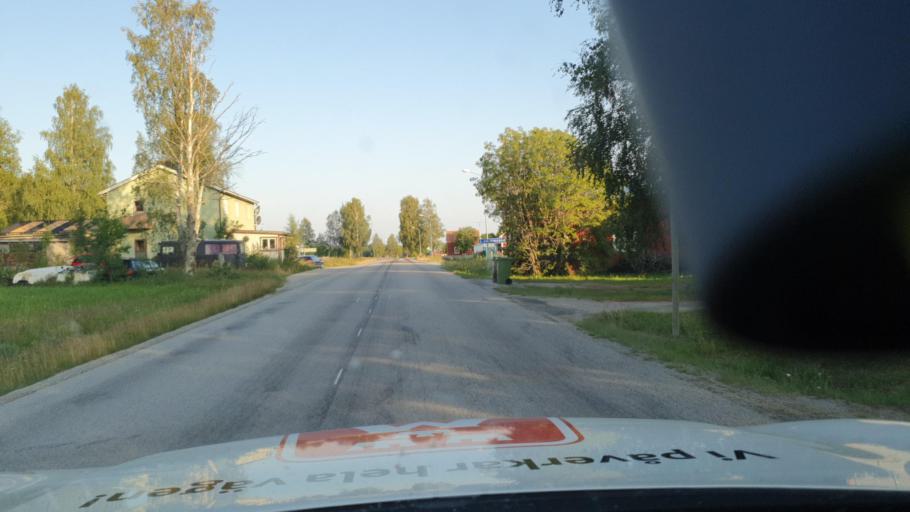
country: SE
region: Vaesterbotten
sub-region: Vindelns Kommun
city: Vindeln
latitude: 64.1394
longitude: 19.5216
